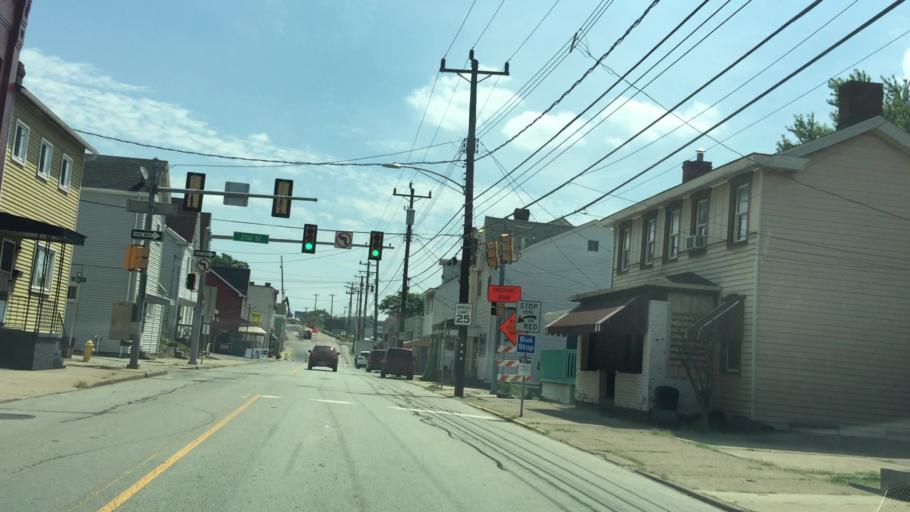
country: US
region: Pennsylvania
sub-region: Allegheny County
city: Sharpsburg
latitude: 40.4937
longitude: -79.9161
